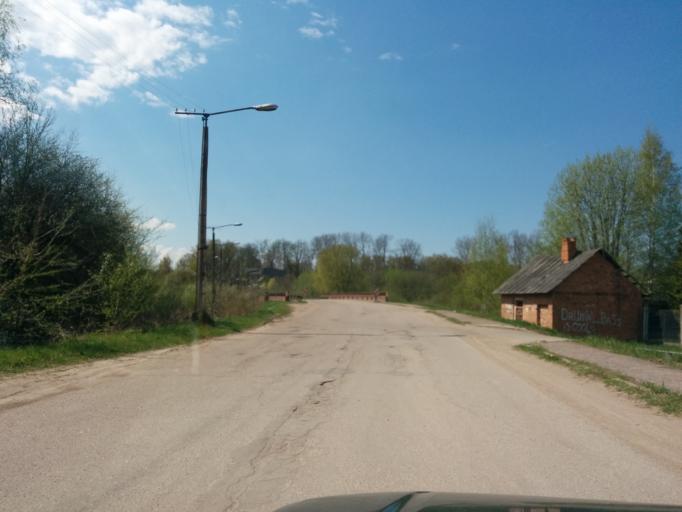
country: LV
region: Ozolnieku
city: Ozolnieki
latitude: 56.6325
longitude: 23.7841
